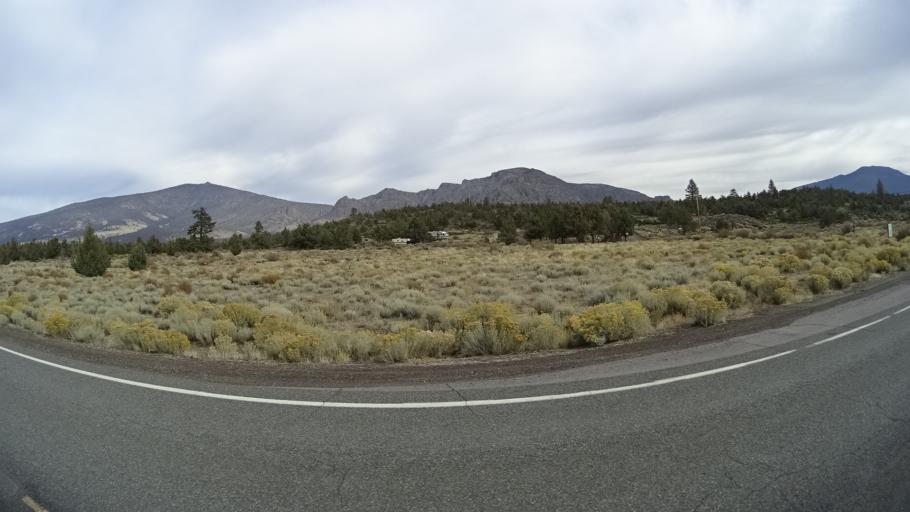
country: US
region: California
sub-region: Siskiyou County
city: Weed
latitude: 41.5653
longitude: -122.2646
